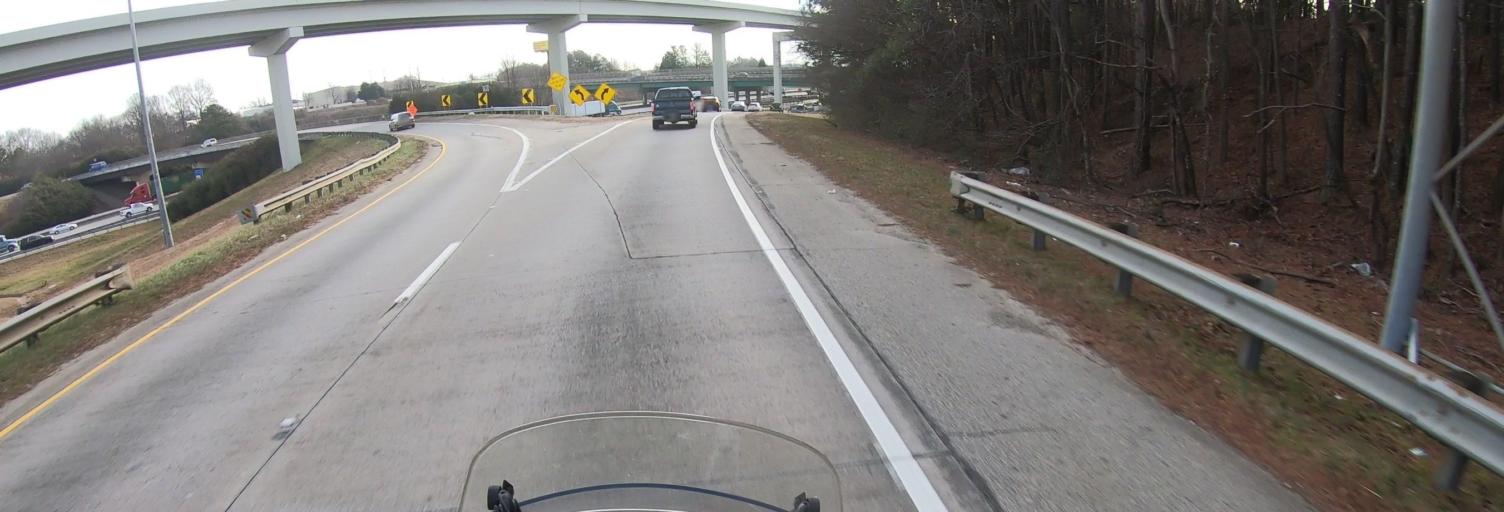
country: US
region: Georgia
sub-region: Cobb County
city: Marietta
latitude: 33.9772
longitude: -84.5445
